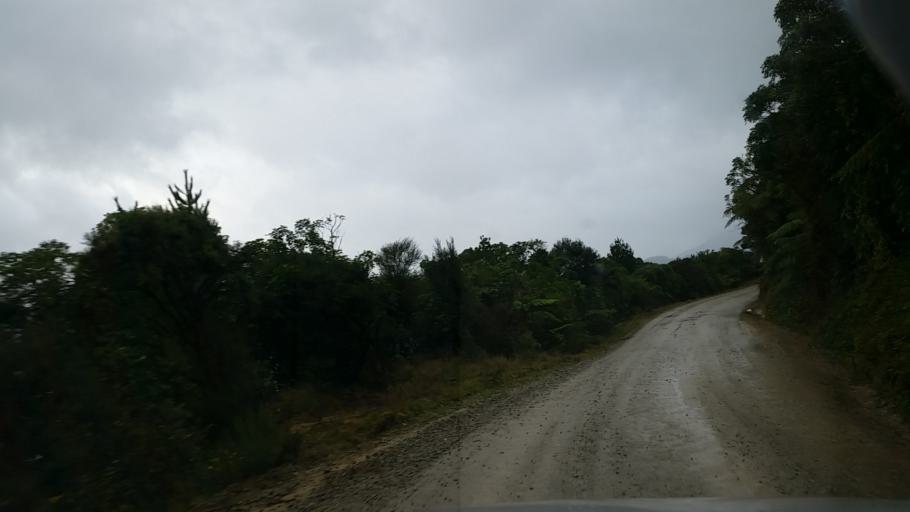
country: NZ
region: Marlborough
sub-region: Marlborough District
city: Picton
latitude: -41.1788
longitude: 174.0539
